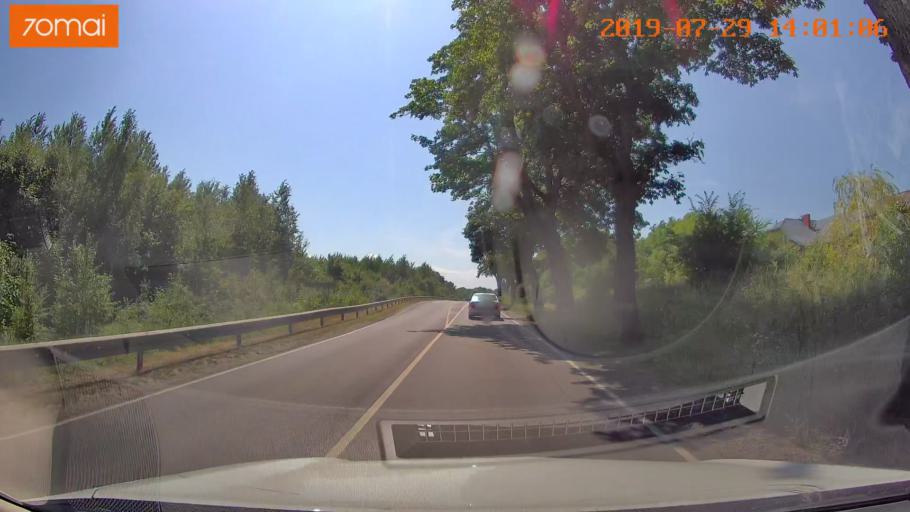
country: RU
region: Kaliningrad
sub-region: Gorod Kaliningrad
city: Baltiysk
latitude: 54.6731
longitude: 19.9241
